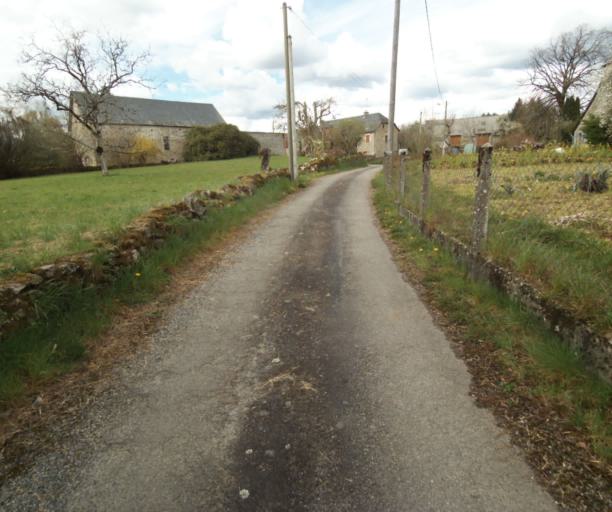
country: FR
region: Limousin
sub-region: Departement de la Correze
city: Argentat
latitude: 45.1982
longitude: 1.9327
